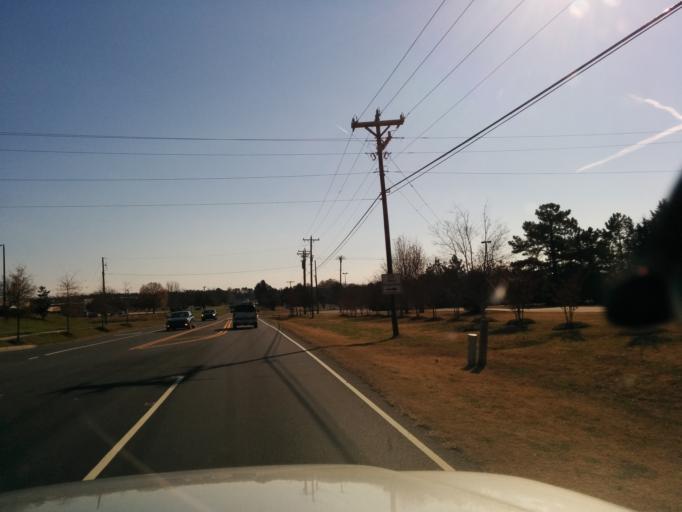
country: US
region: North Carolina
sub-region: Iredell County
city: Mooresville
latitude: 35.5959
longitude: -80.8383
